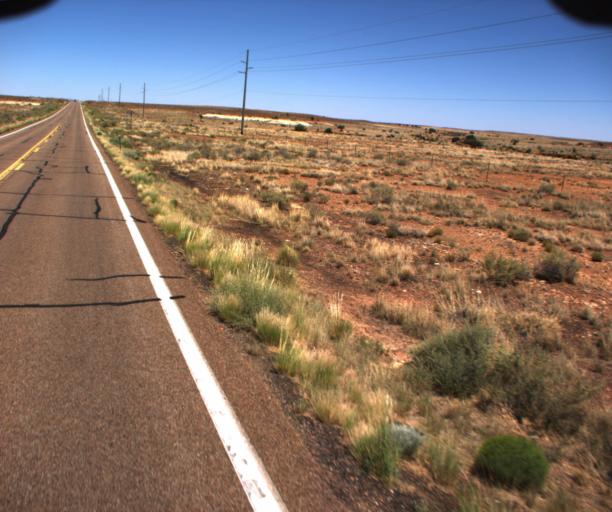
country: US
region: Arizona
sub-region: Coconino County
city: LeChee
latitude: 34.9092
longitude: -110.8389
